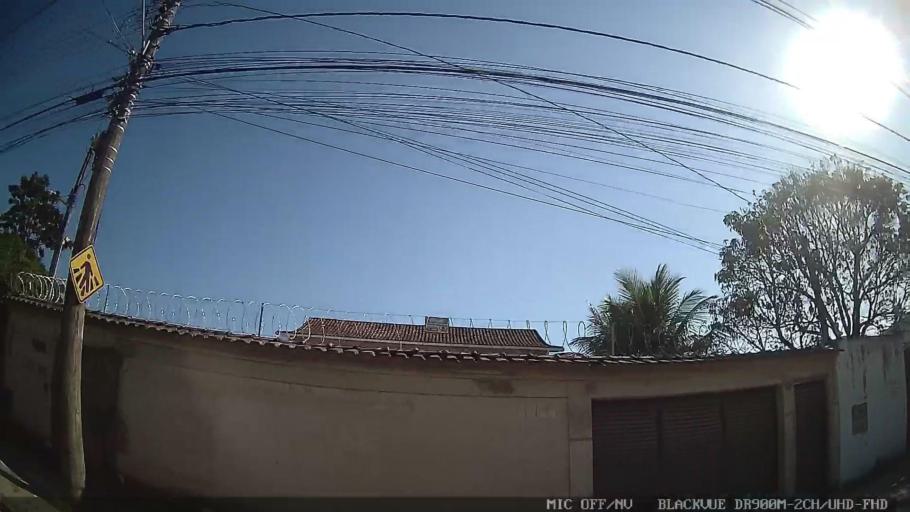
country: BR
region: Sao Paulo
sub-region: Guaruja
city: Guaruja
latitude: -23.9689
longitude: -46.2112
